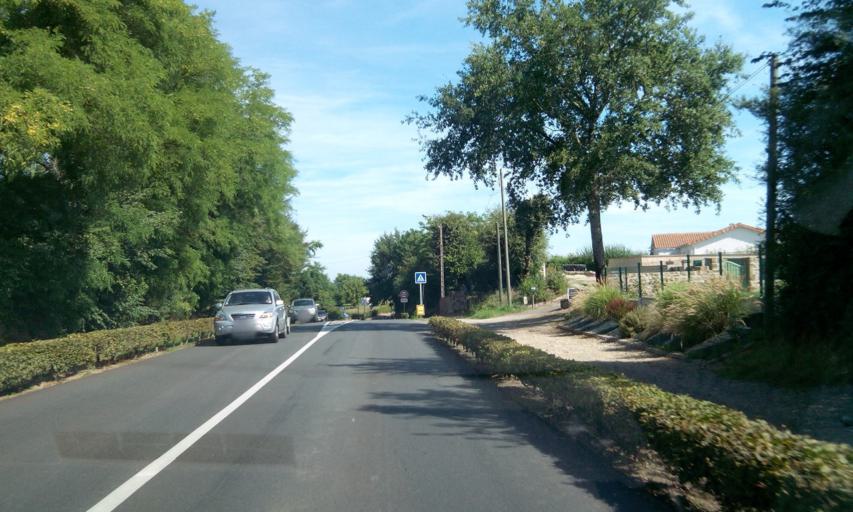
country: FR
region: Poitou-Charentes
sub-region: Departement de la Charente
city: Confolens
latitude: 45.9617
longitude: 0.7012
